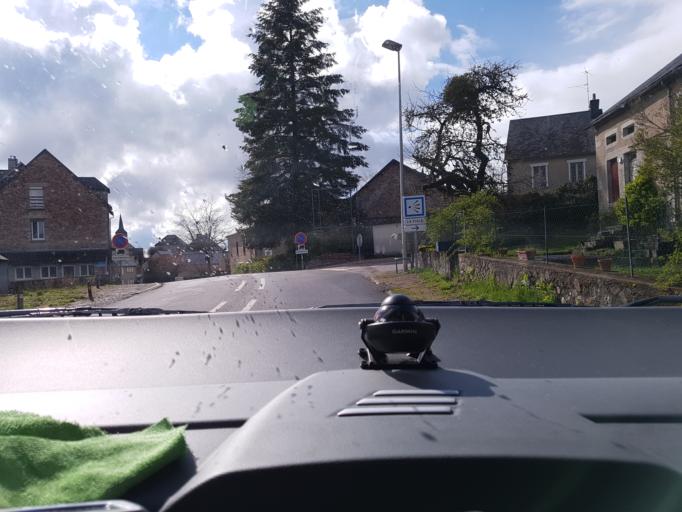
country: FR
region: Bourgogne
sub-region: Departement de la Nievre
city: Chateau-Chinon(Ville)
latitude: 47.1366
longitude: 4.0179
